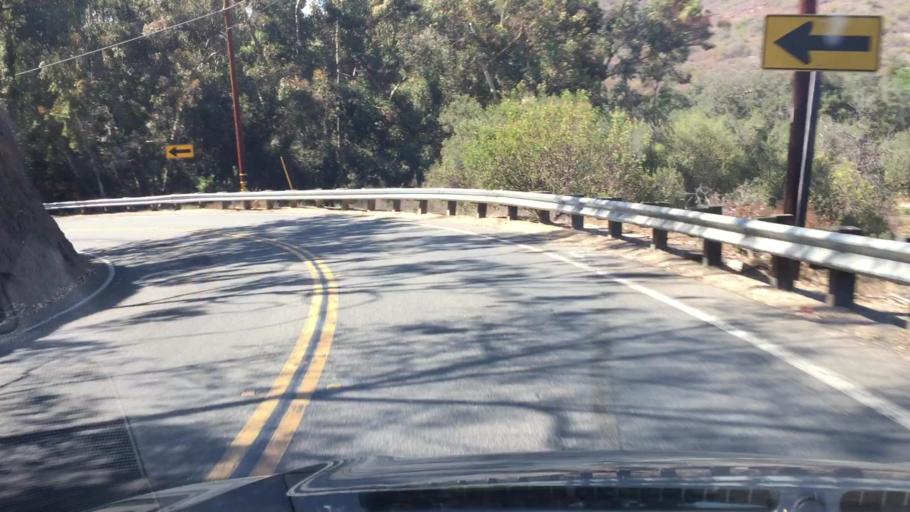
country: US
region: California
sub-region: San Diego County
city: Jamul
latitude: 32.7282
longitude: -116.8704
